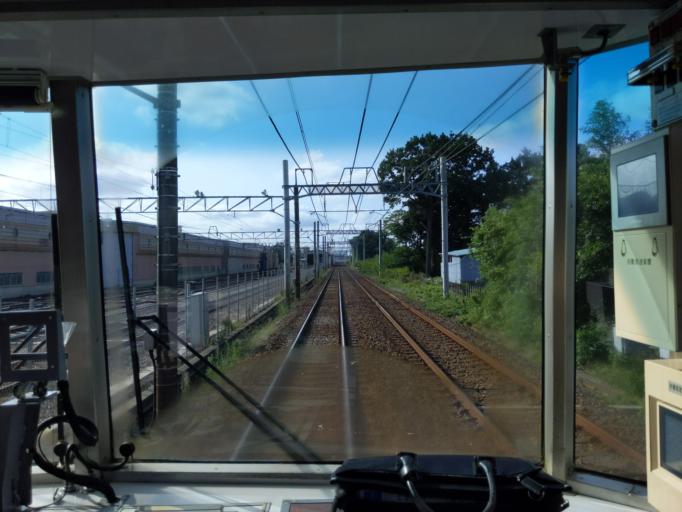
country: JP
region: Chiba
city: Kashiwa
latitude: 35.7774
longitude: 139.9819
